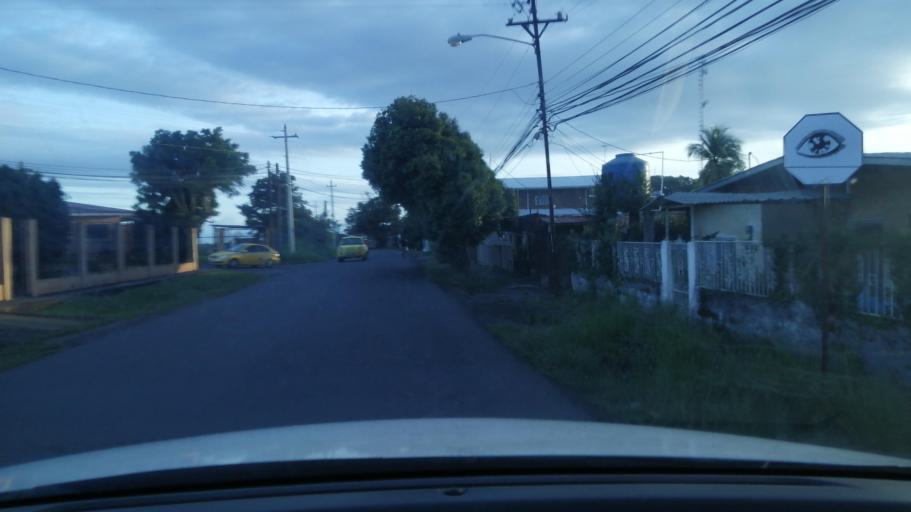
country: PA
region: Chiriqui
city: David
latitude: 8.4086
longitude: -82.4341
